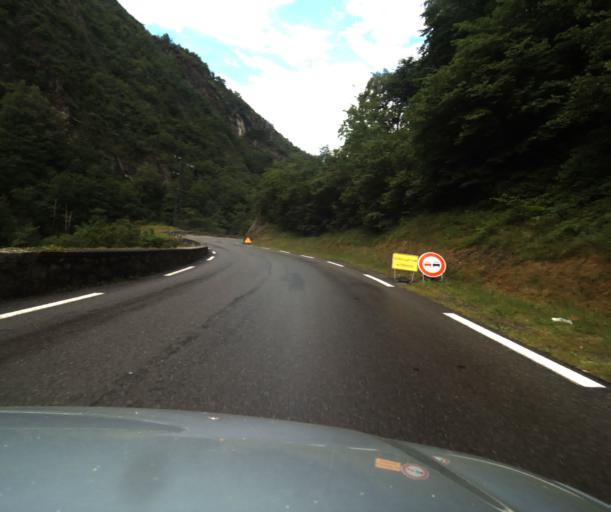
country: FR
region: Midi-Pyrenees
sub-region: Departement des Hautes-Pyrenees
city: Luz-Saint-Sauveur
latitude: 42.8512
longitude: -0.0072
